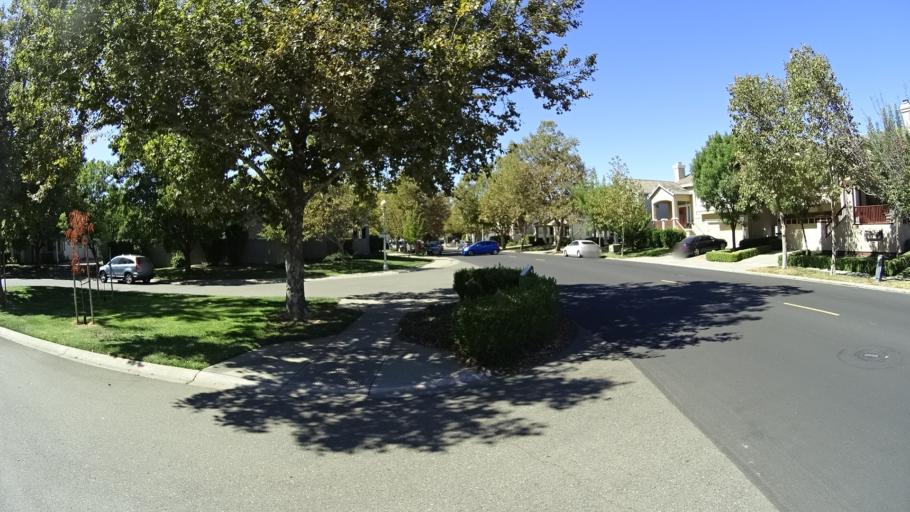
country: US
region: California
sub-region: Sacramento County
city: Laguna
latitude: 38.4174
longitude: -121.4678
